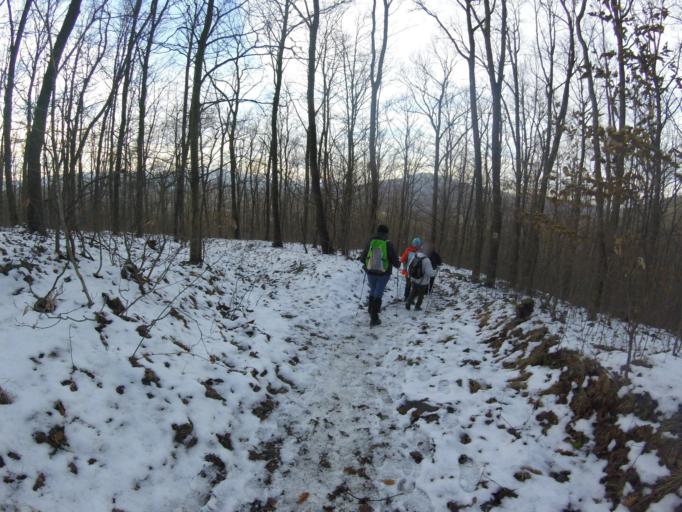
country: HU
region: Pest
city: Visegrad
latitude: 47.7271
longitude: 18.9960
